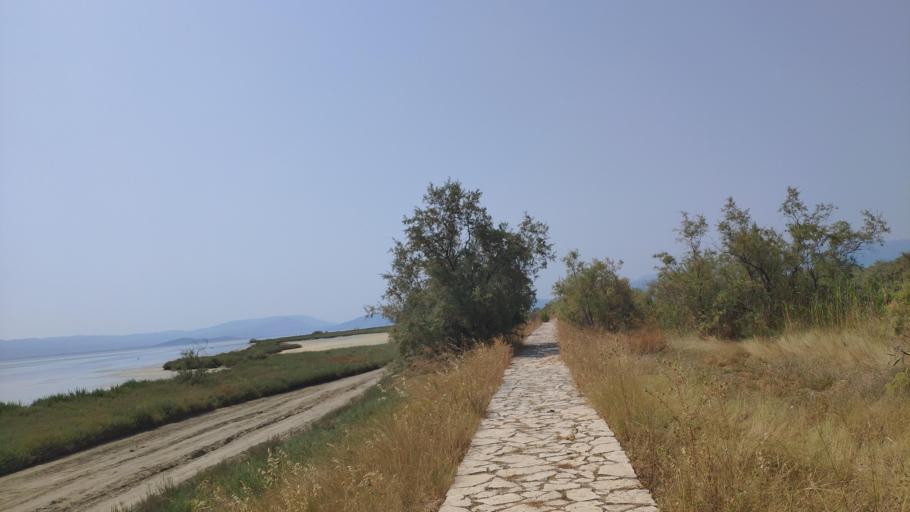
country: GR
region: West Greece
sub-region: Nomos Aitolias kai Akarnanias
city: Menidi
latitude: 39.0362
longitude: 21.0746
